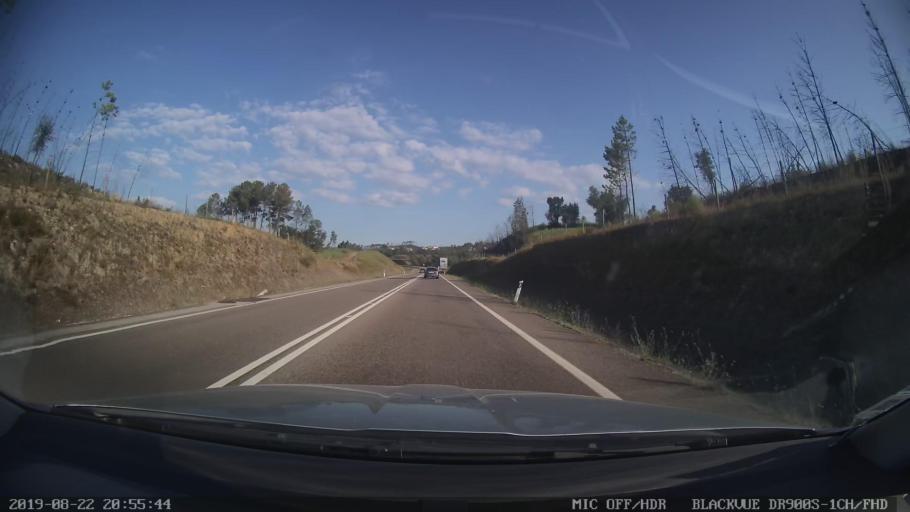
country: PT
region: Castelo Branco
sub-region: Serta
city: Serta
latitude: 39.7827
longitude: -8.0386
